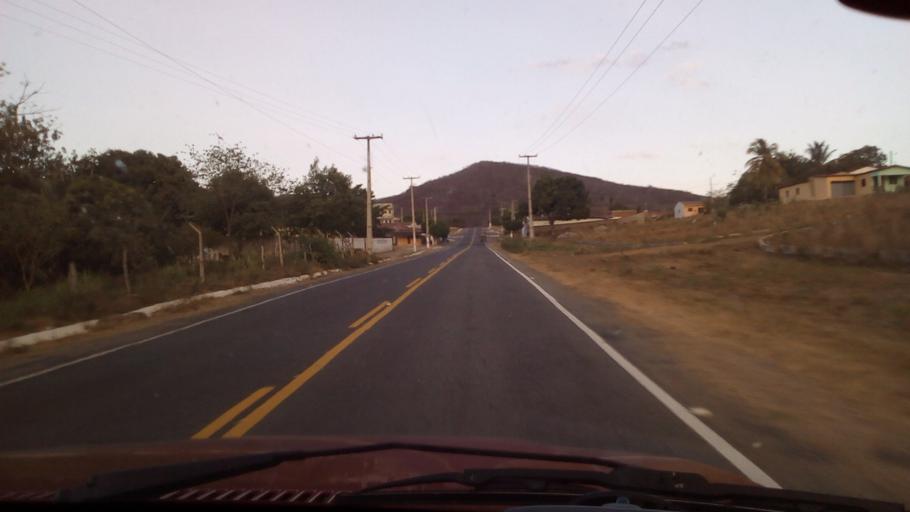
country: BR
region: Paraiba
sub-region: Belem
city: Belem
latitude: -6.7210
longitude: -35.5436
